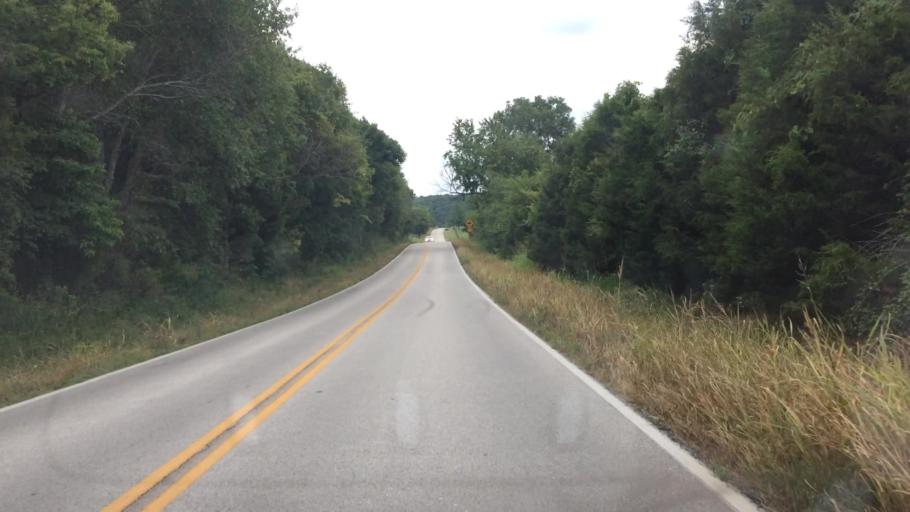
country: US
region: Missouri
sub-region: Greene County
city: Strafford
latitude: 37.2867
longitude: -93.0973
